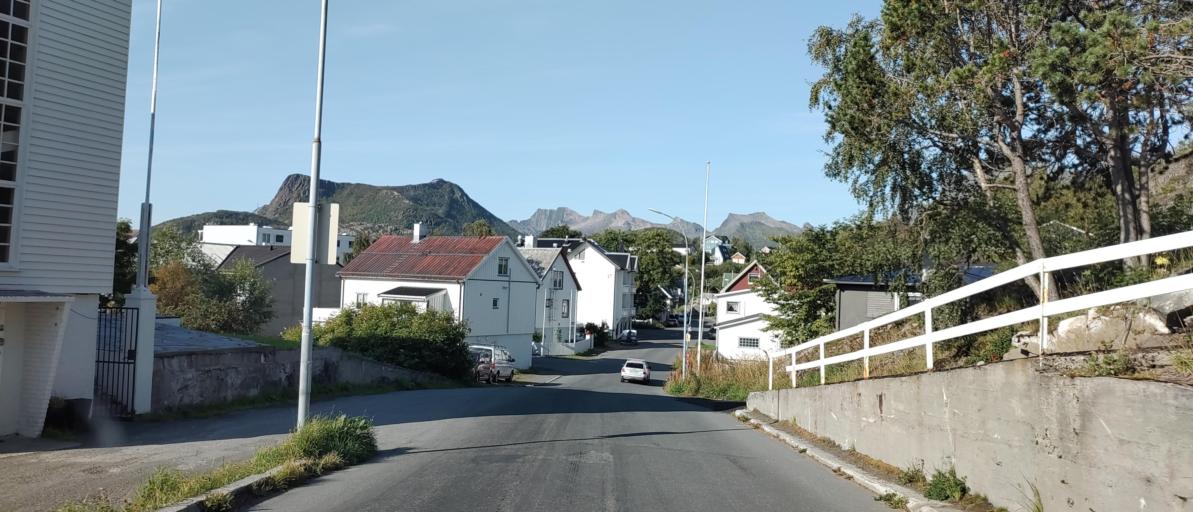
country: NO
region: Nordland
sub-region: Vagan
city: Svolvaer
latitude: 68.2369
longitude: 14.5722
